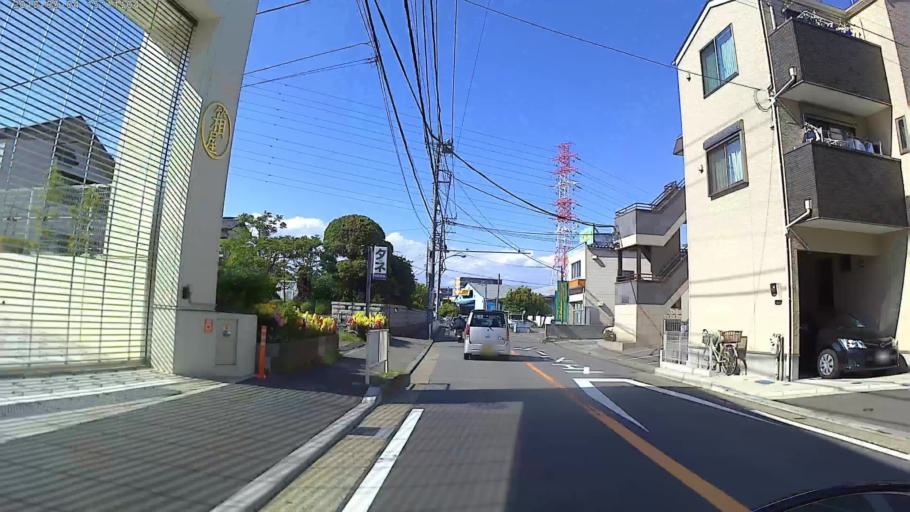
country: JP
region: Kanagawa
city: Yokohama
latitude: 35.5234
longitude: 139.6104
